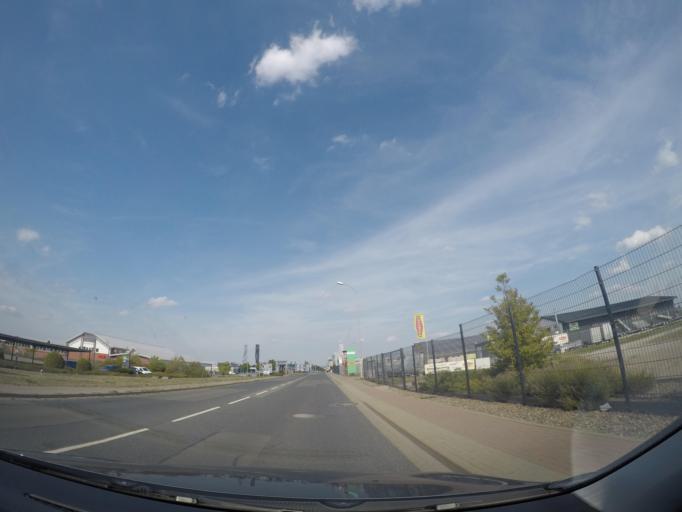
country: DE
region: Saxony-Anhalt
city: Wernigerode
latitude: 51.8502
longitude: 10.7873
